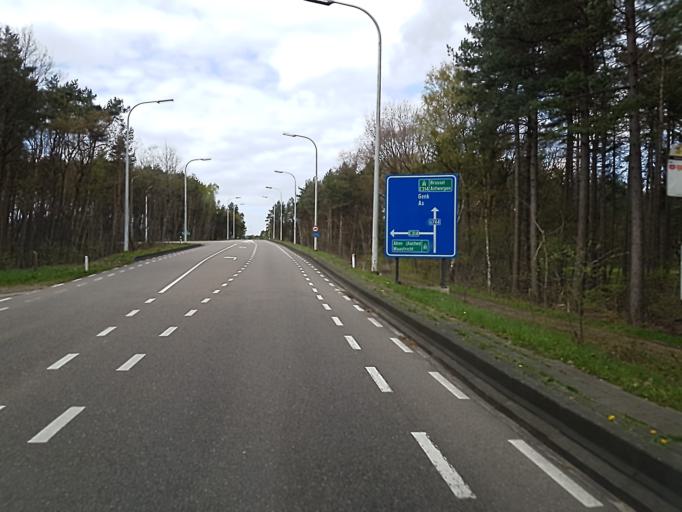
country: BE
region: Flanders
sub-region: Provincie Limburg
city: Zutendaal
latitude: 50.9734
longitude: 5.5524
